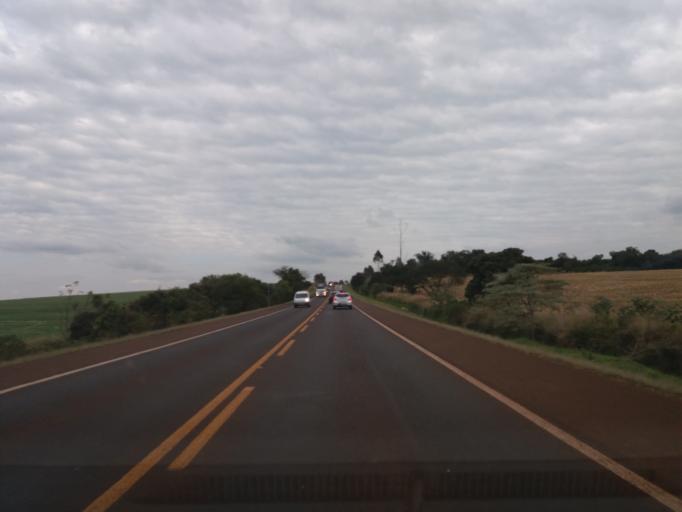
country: BR
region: Parana
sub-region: Corbelia
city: Corbelia
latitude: -24.8761
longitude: -53.3430
